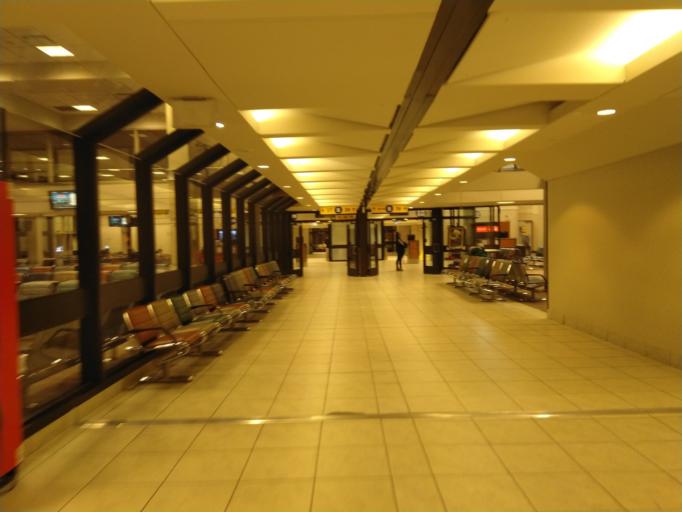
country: CA
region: Alberta
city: Calgary
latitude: 51.1299
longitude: -114.0118
